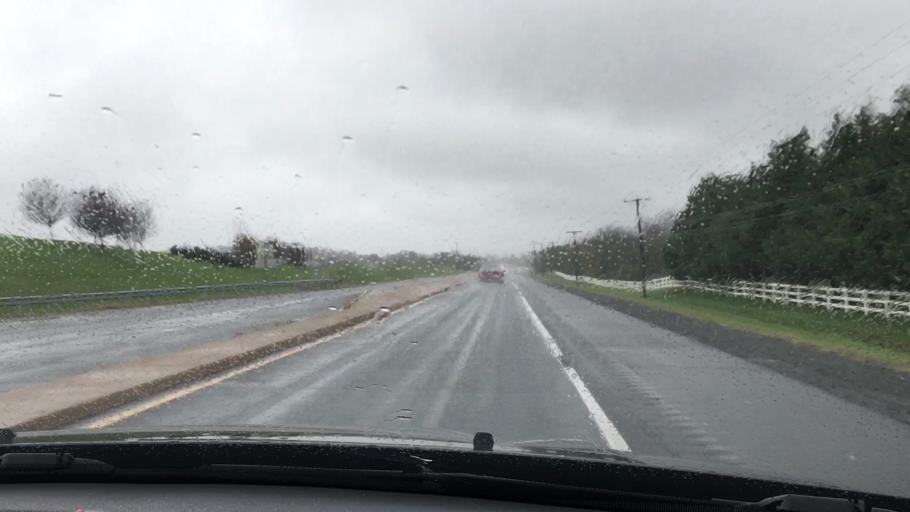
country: US
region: Virginia
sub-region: Loudoun County
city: Leesburg
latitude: 39.1518
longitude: -77.5407
